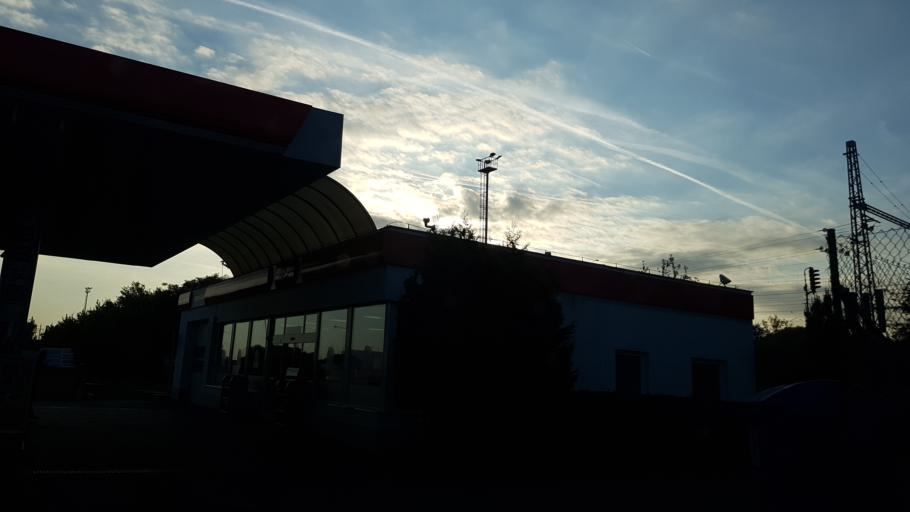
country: CZ
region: Zlin
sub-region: Okres Uherske Hradiste
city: Stare Mesto
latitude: 49.0744
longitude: 17.4221
